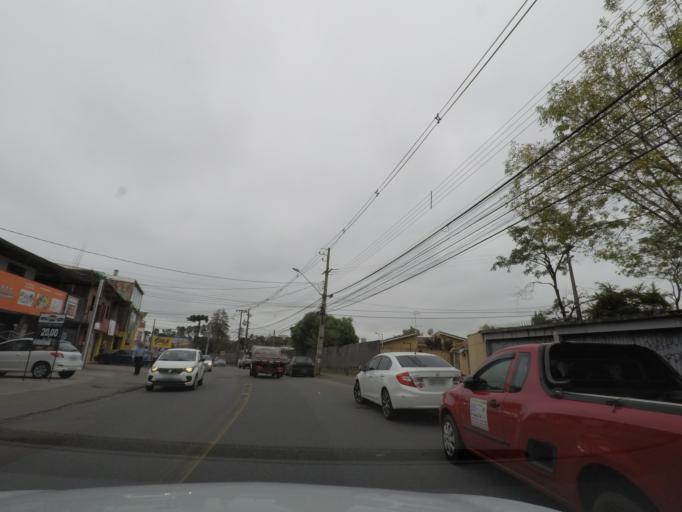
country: BR
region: Parana
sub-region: Curitiba
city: Curitiba
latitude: -25.4593
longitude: -49.3455
